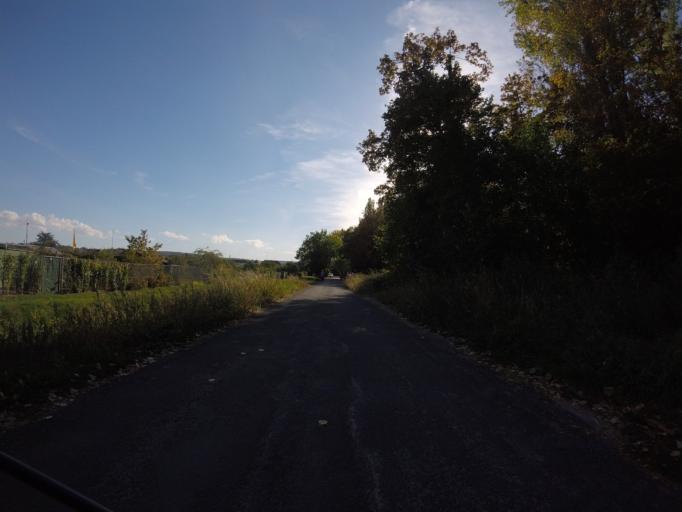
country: DE
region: Baden-Wuerttemberg
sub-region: Karlsruhe Region
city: Karlsruhe
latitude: 49.0067
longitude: 8.4598
